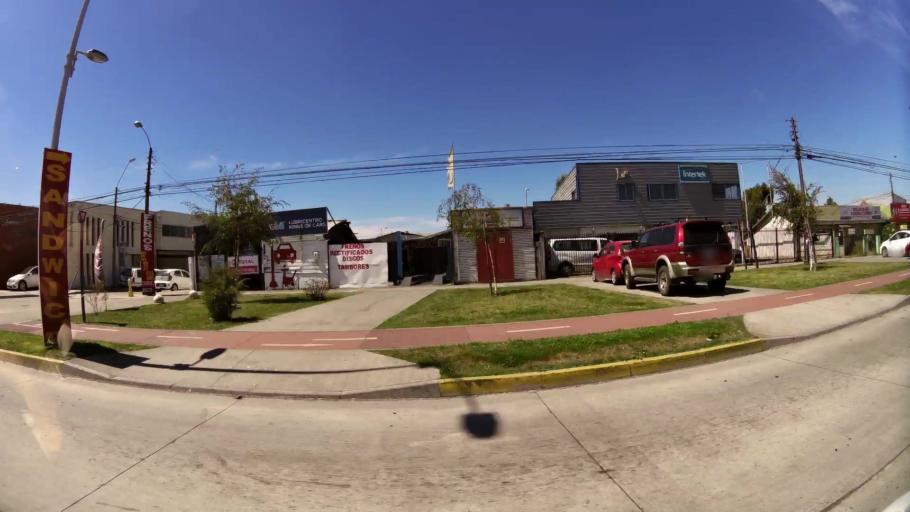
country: CL
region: Biobio
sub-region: Provincia de Concepcion
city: Talcahuano
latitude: -36.7463
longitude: -73.0951
